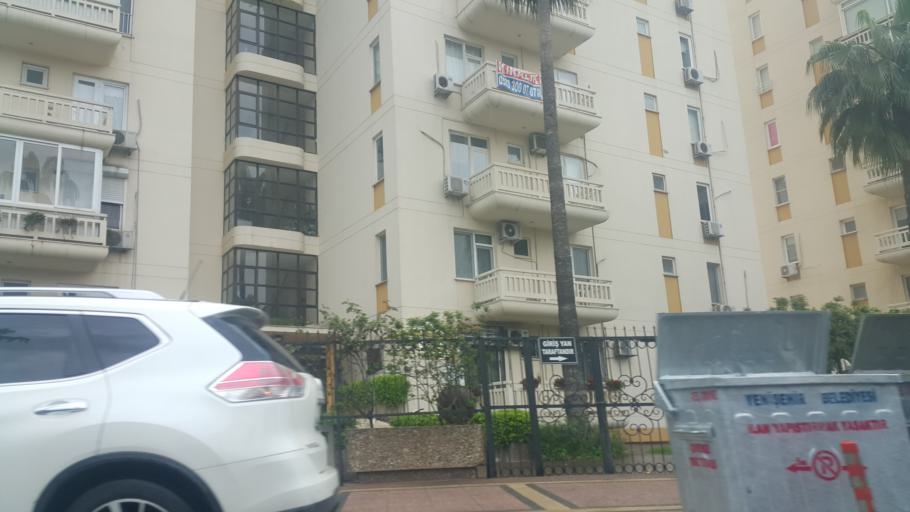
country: TR
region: Mersin
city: Mercin
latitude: 36.7837
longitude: 34.6133
